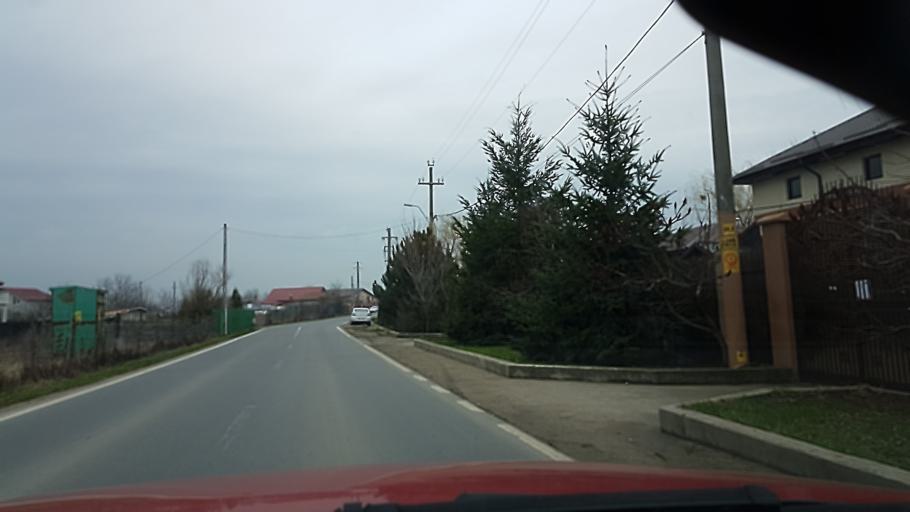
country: RO
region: Ilfov
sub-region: Comuna Balotesti
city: Balotesti
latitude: 44.5884
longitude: 26.1365
